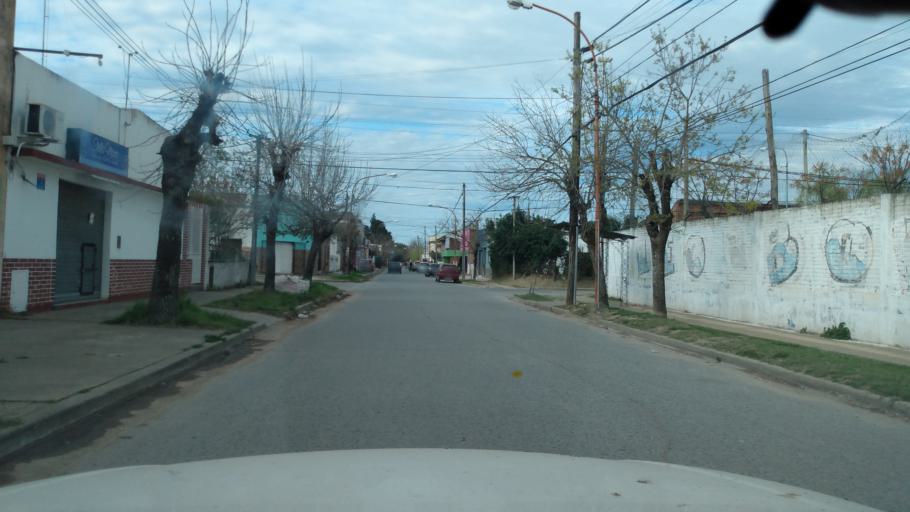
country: AR
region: Buenos Aires
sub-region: Partido de Lujan
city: Lujan
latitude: -34.5677
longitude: -59.1319
